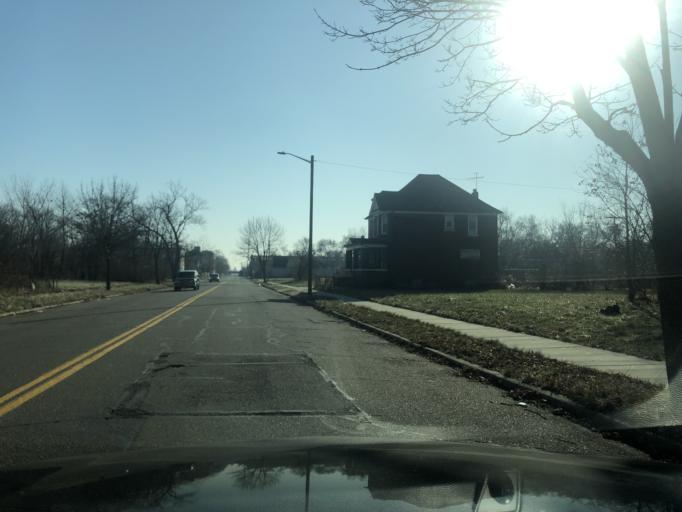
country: US
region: Michigan
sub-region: Wayne County
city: Detroit
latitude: 42.3369
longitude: -83.1054
